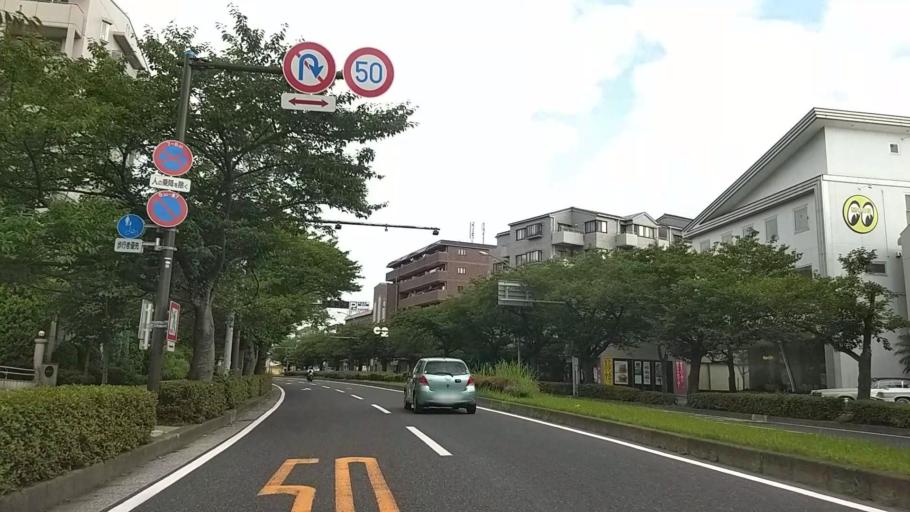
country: JP
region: Kanagawa
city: Yokohama
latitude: 35.4281
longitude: 139.6652
